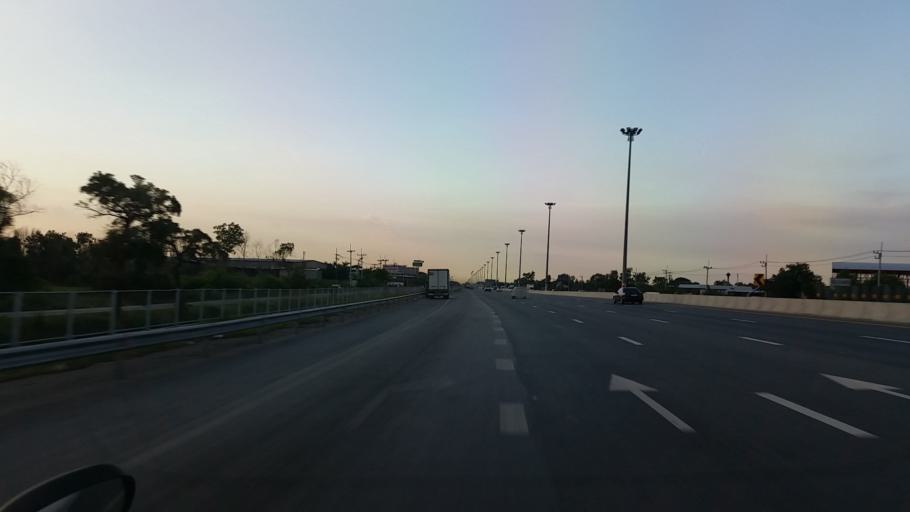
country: TH
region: Pathum Thani
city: Khlong Luang
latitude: 14.0876
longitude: 100.6938
